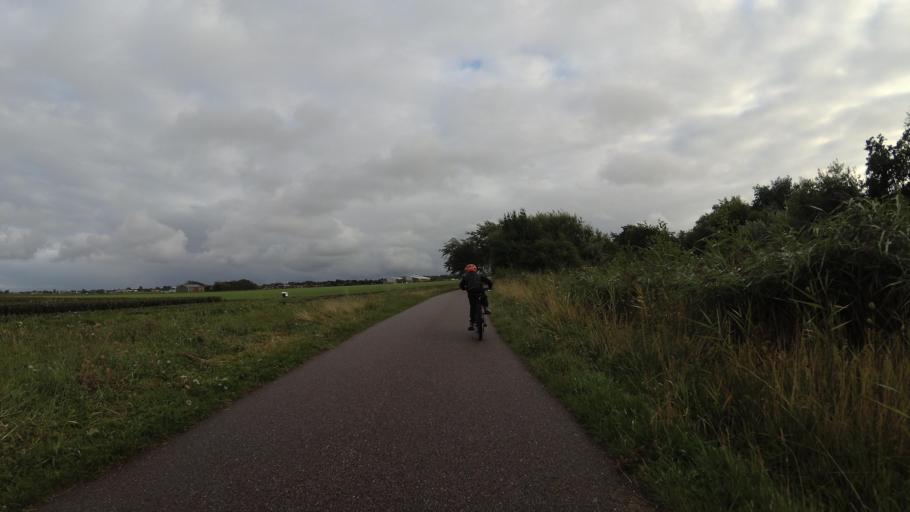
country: NL
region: North Holland
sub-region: Gemeente Den Helder
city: Den Helder
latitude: 52.9079
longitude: 4.7284
